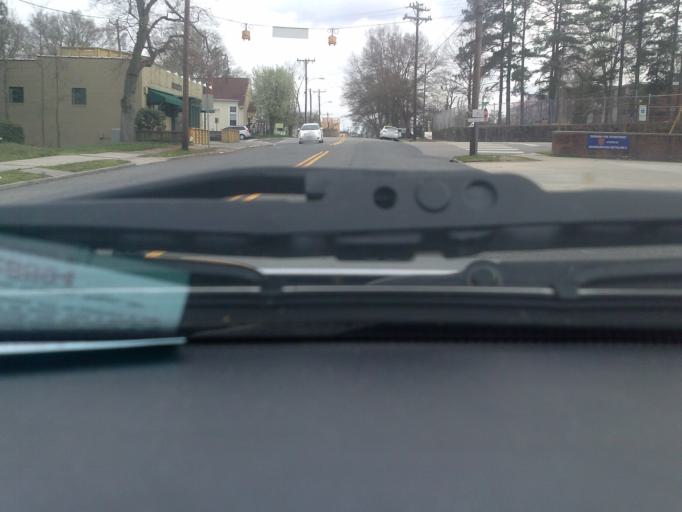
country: US
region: North Carolina
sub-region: Durham County
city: Durham
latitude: 36.0143
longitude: -78.9218
